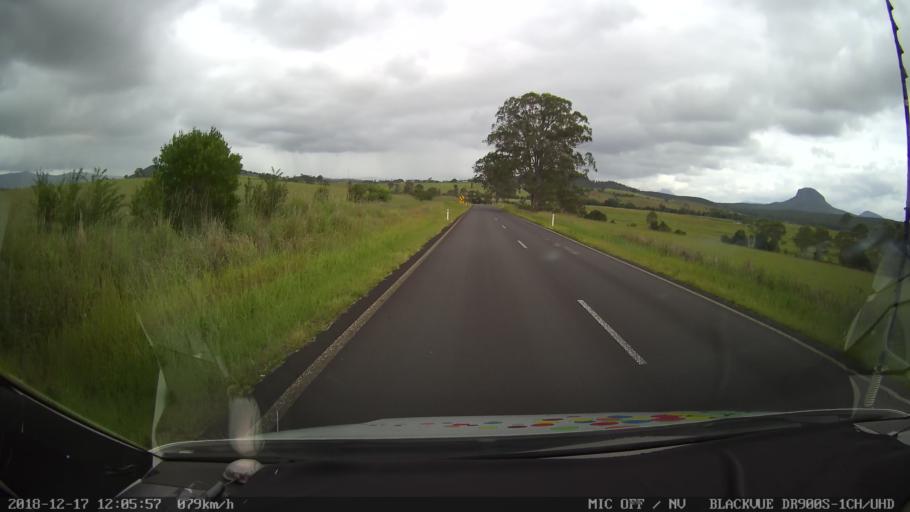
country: AU
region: New South Wales
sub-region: Kyogle
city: Kyogle
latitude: -28.4871
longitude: 152.5675
